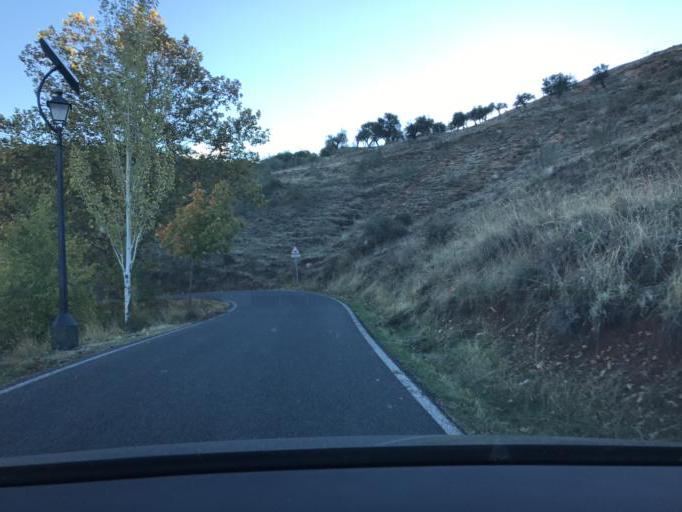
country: ES
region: Andalusia
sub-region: Provincia de Granada
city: Viznar
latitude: 37.2357
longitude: -3.5491
